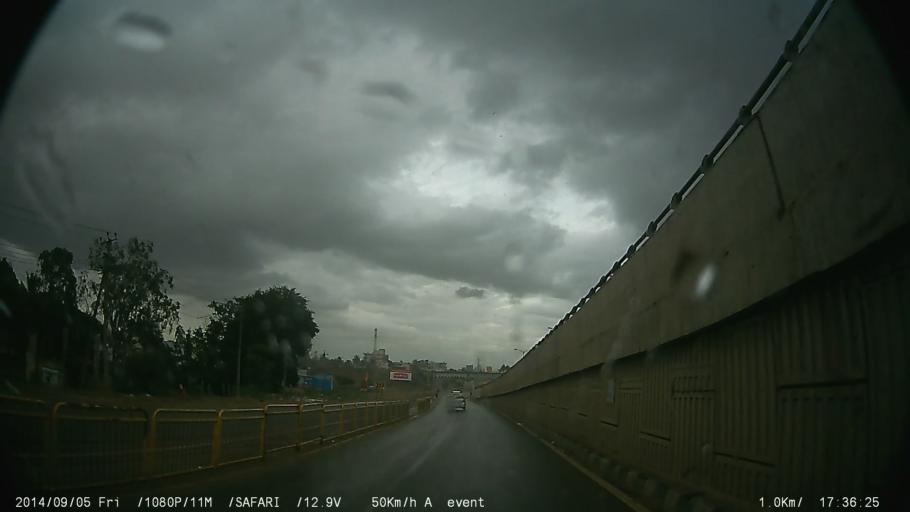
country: IN
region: Karnataka
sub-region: Bangalore Urban
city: Anekal
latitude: 12.8022
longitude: 77.7071
